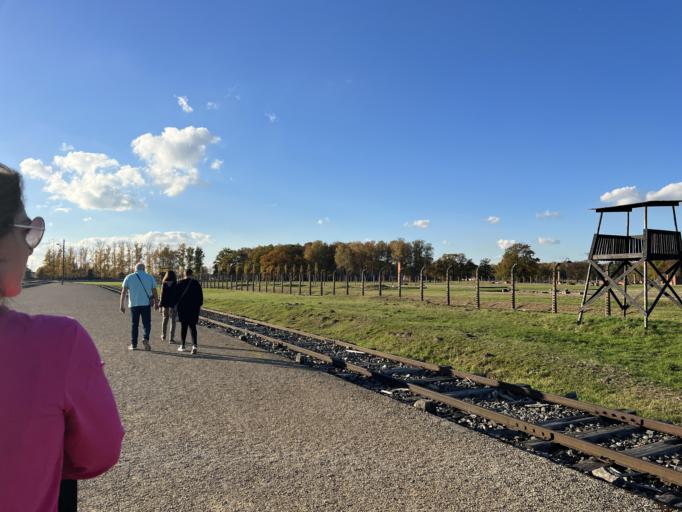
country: PL
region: Lesser Poland Voivodeship
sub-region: Powiat oswiecimski
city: Brzezinka
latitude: 50.0348
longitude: 19.1742
